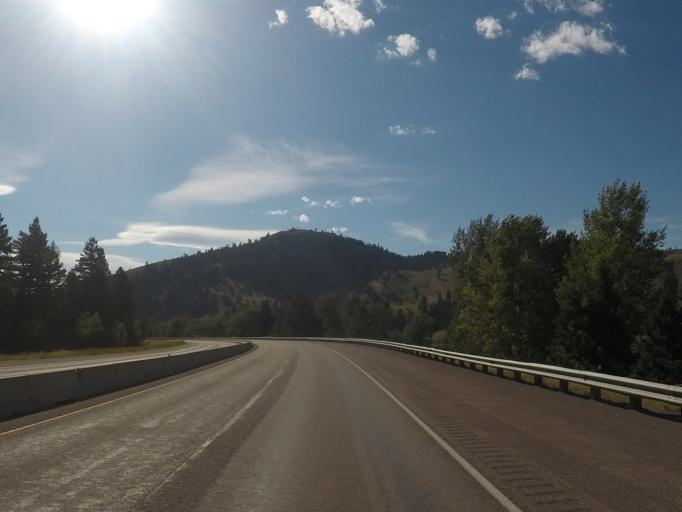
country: US
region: Montana
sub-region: Granite County
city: Philipsburg
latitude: 46.7179
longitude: -113.2919
